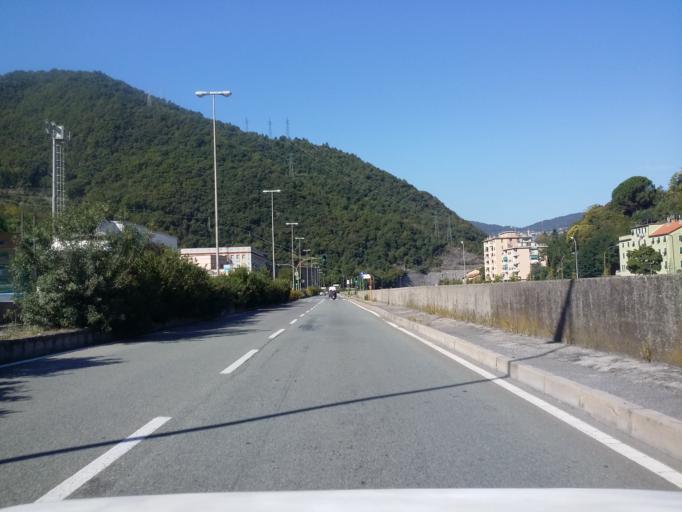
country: IT
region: Liguria
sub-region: Provincia di Genova
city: Piccarello
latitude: 44.4479
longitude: 8.9981
